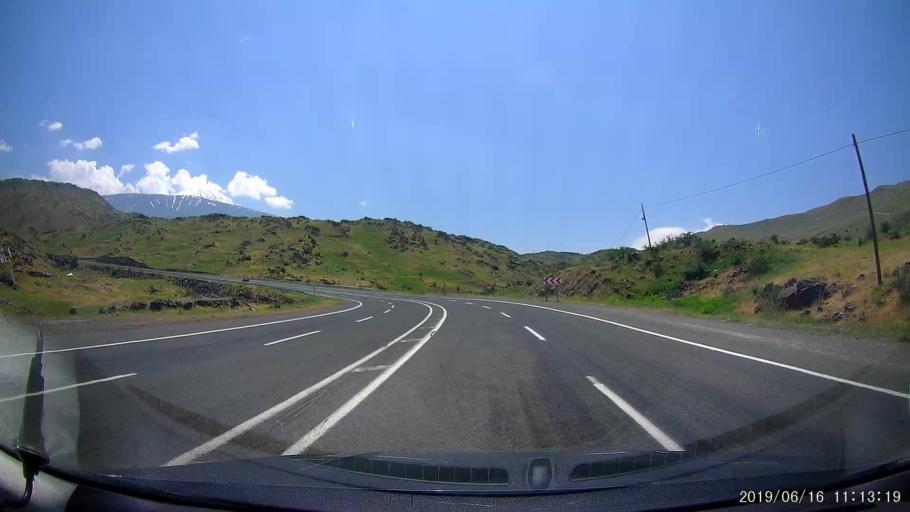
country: TR
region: Igdir
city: Igdir
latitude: 39.7855
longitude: 44.1357
